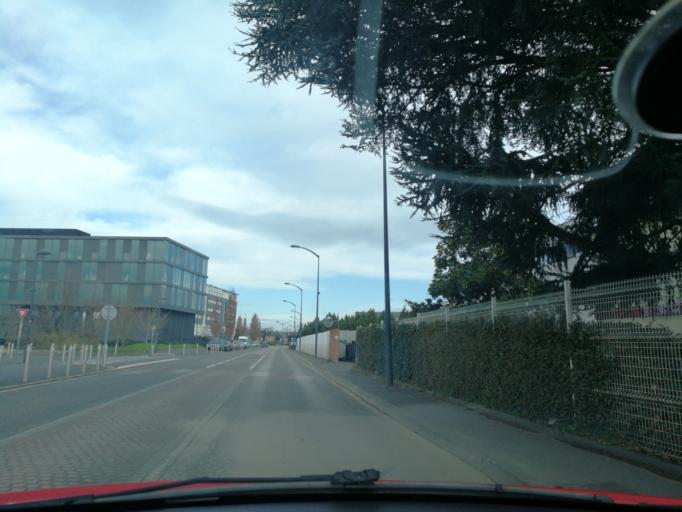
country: FR
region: Midi-Pyrenees
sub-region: Departement de la Haute-Garonne
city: Balma
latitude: 43.6257
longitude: 1.4850
